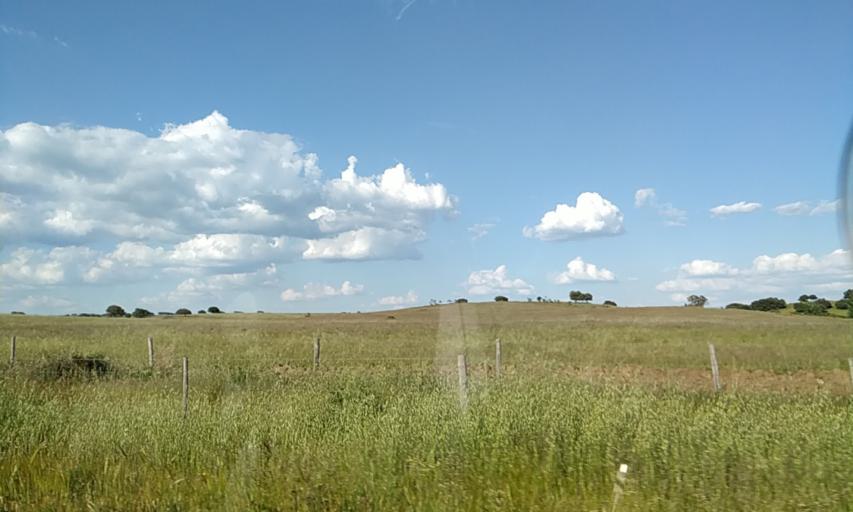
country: PT
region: Portalegre
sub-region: Portalegre
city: Urra
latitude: 39.1188
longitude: -7.4415
